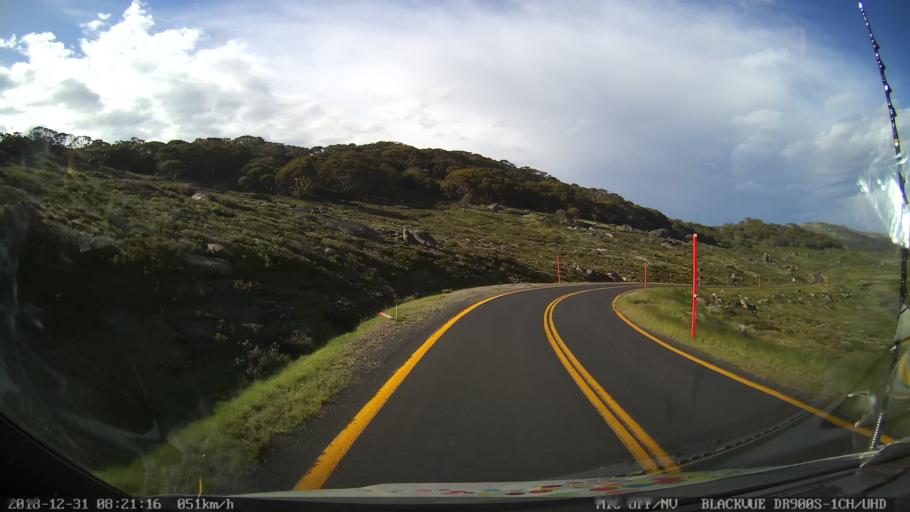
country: AU
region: New South Wales
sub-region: Snowy River
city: Jindabyne
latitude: -36.4269
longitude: 148.3691
